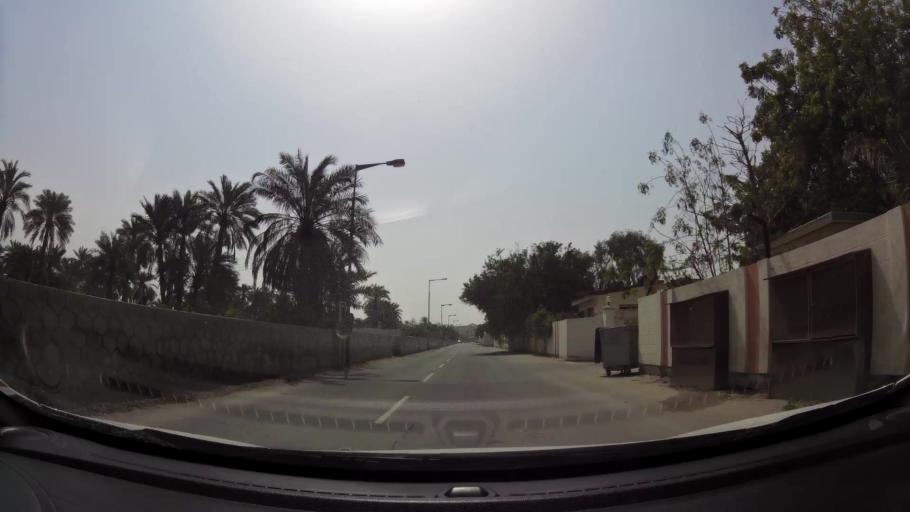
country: BH
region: Manama
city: Jidd Hafs
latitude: 26.2246
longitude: 50.5041
